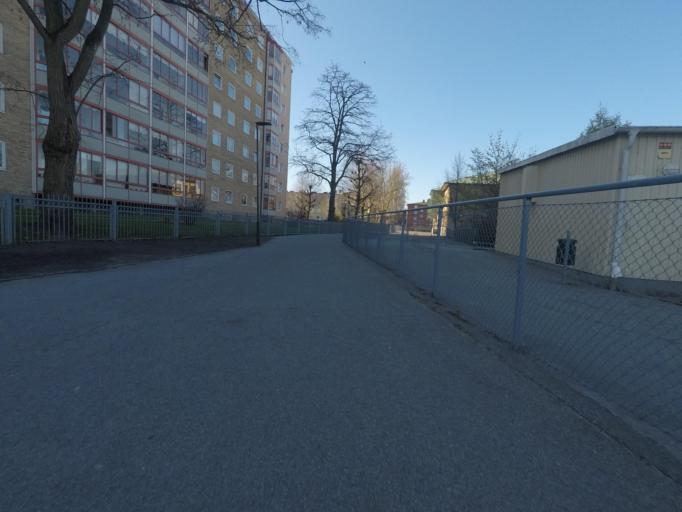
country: SE
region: Skane
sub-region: Malmo
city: Malmoe
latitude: 55.5717
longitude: 13.0192
